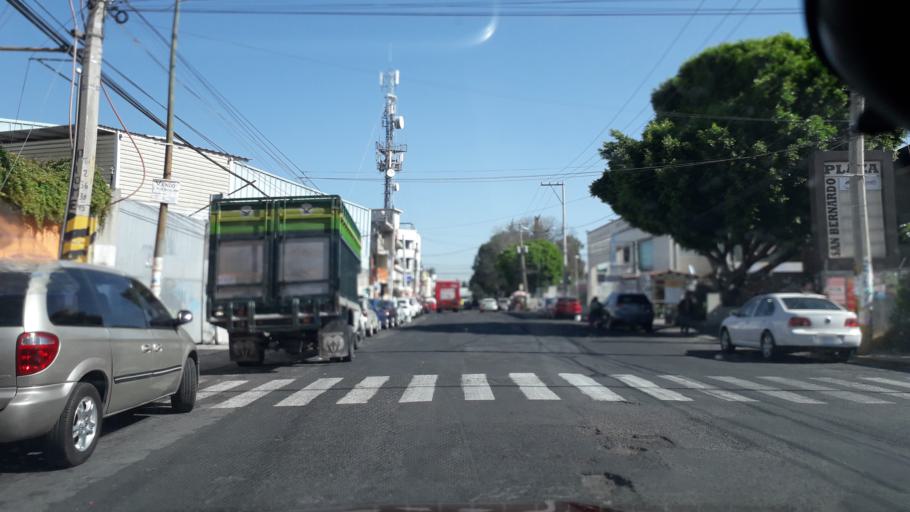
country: MX
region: Puebla
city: Puebla
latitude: 19.0754
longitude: -98.2112
